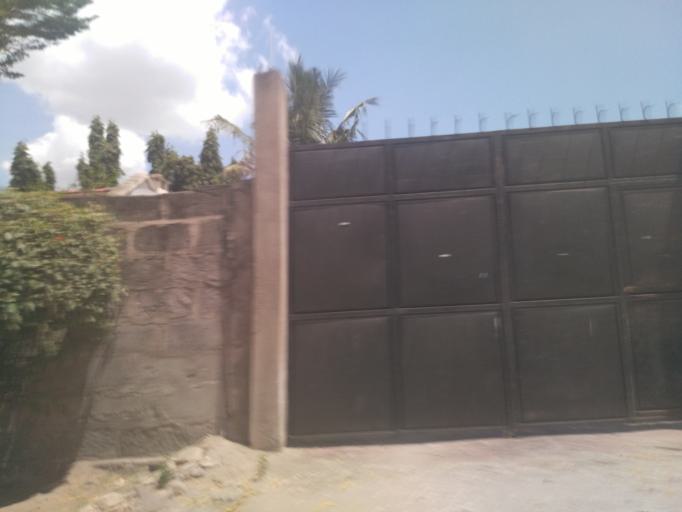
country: TZ
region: Dar es Salaam
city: Dar es Salaam
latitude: -6.8440
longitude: 39.2657
